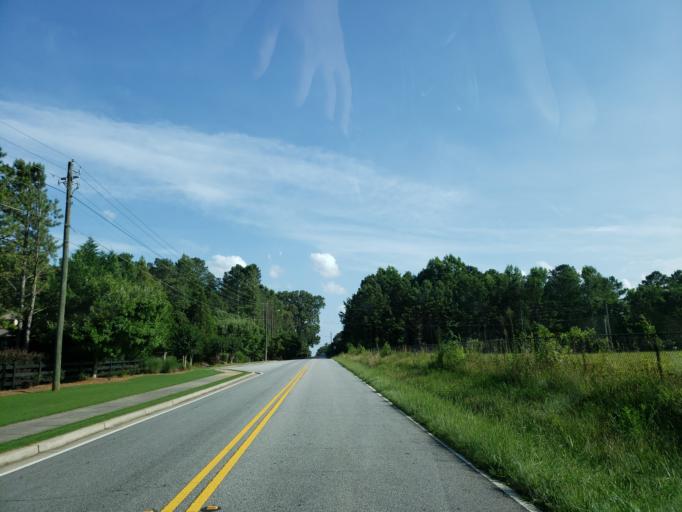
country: US
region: Georgia
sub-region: Cobb County
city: Powder Springs
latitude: 33.9270
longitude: -84.7057
